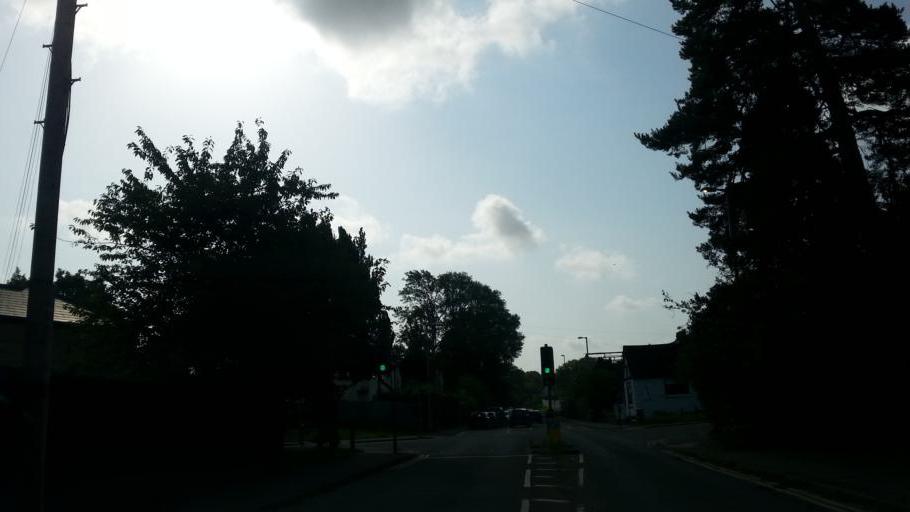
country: GB
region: England
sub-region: Cambridgeshire
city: Papworth Everard
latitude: 52.2495
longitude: -0.1182
